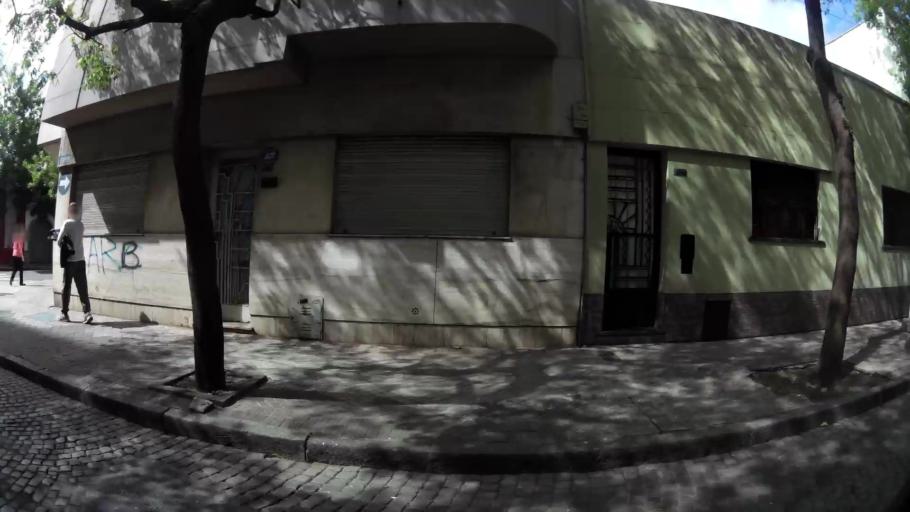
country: AR
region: Santa Fe
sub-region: Departamento de Rosario
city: Rosario
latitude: -32.9536
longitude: -60.6488
